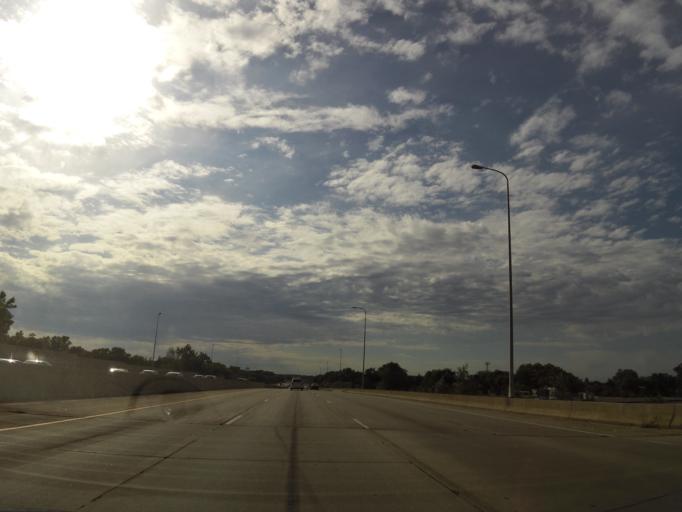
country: US
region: Minnesota
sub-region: Hennepin County
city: Brooklyn Park
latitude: 45.0782
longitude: -93.3744
